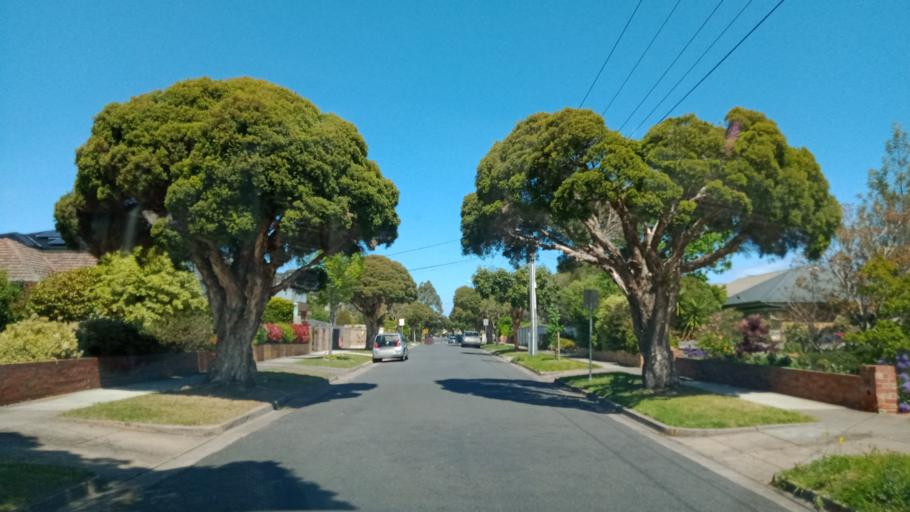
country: AU
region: Victoria
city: McKinnon
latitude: -37.9097
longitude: 145.0540
